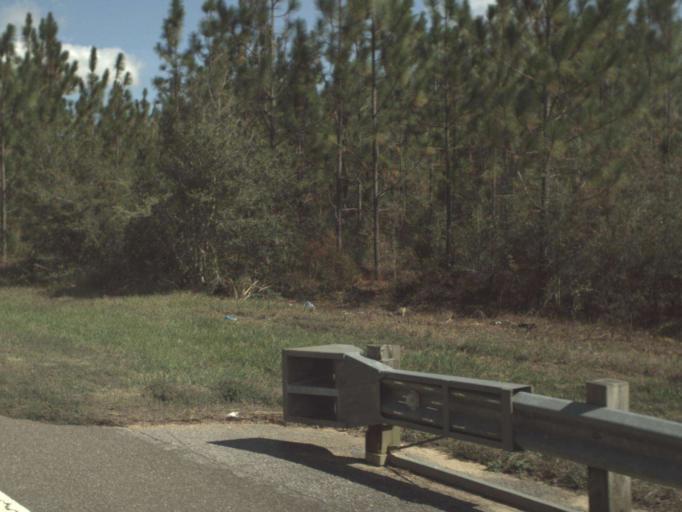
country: US
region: Alabama
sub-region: Geneva County
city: Samson
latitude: 30.9407
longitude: -86.1373
